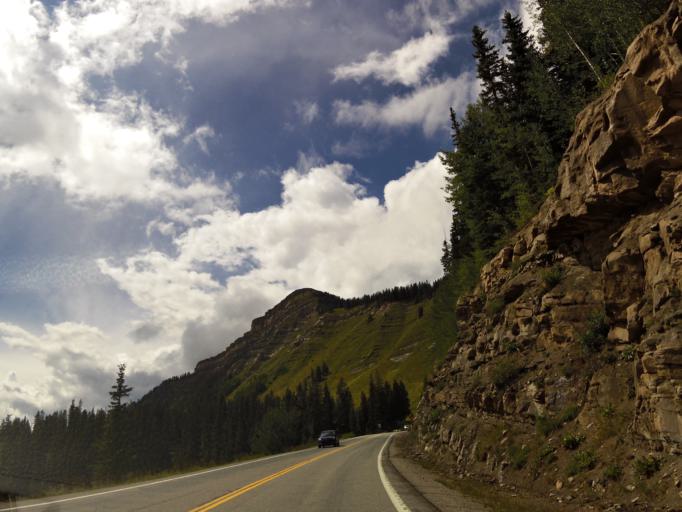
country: US
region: Colorado
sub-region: San Juan County
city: Silverton
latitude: 37.7004
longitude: -107.7738
